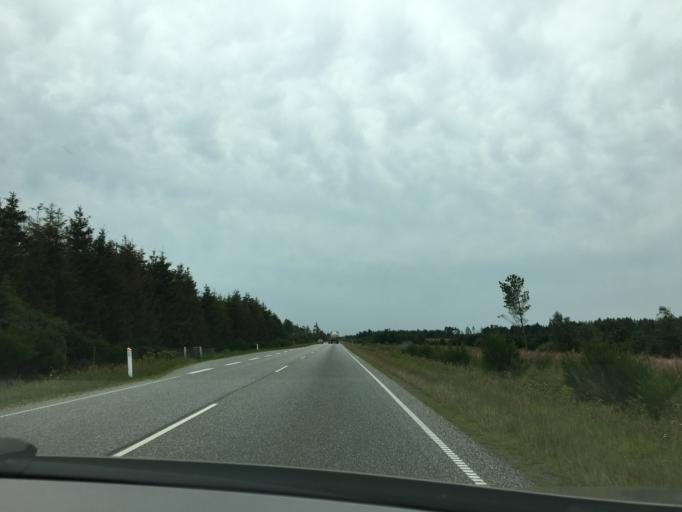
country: DK
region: Central Jutland
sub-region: Herning Kommune
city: Sunds
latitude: 56.3496
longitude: 8.9746
